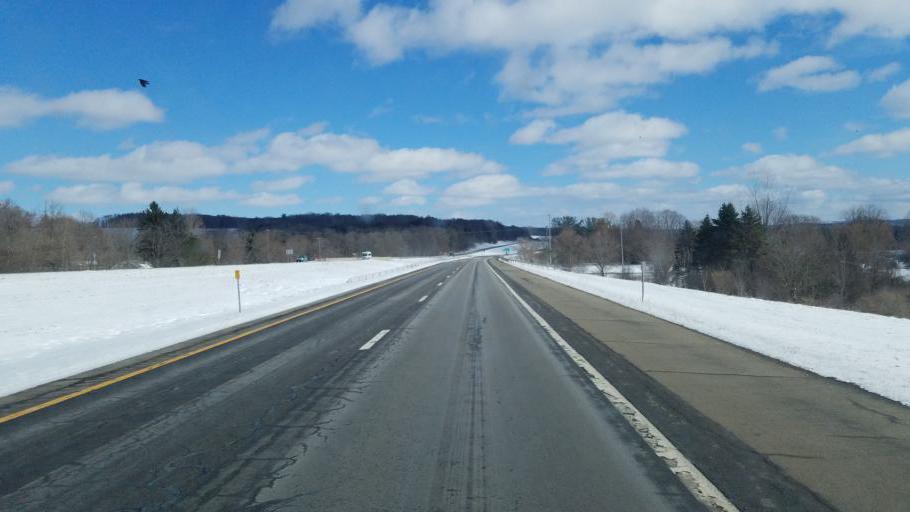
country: US
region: New York
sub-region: Chautauqua County
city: Celoron
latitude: 42.1280
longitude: -79.2982
